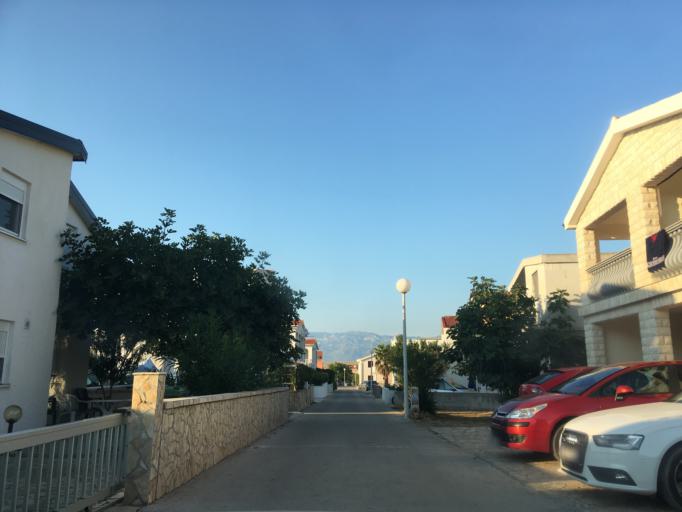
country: HR
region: Zadarska
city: Vir
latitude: 44.3046
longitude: 15.0994
